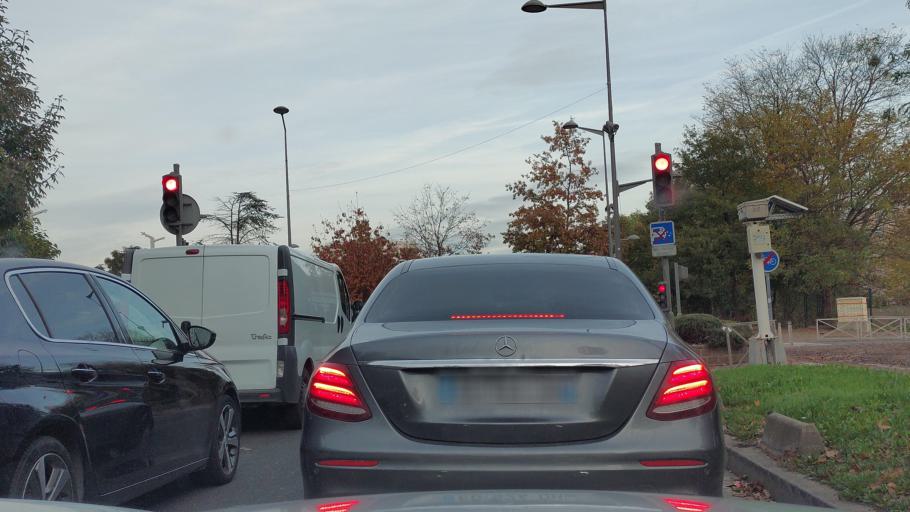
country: FR
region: Ile-de-France
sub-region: Departement de Seine-Saint-Denis
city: Aulnay-sous-Bois
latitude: 48.9522
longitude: 2.4941
